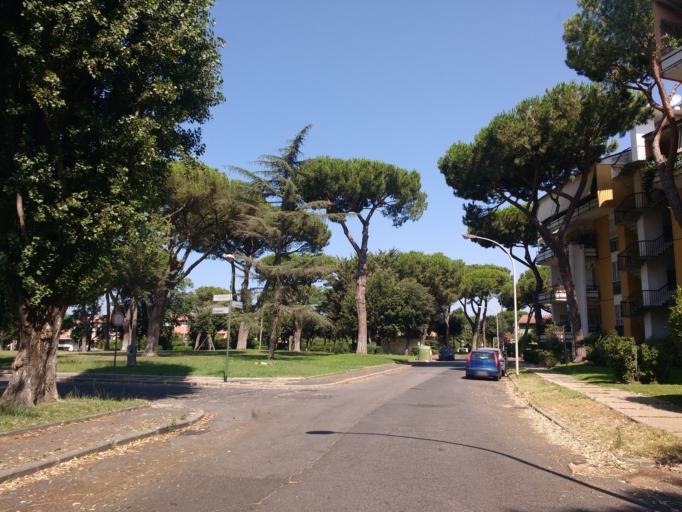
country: IT
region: Latium
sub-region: Citta metropolitana di Roma Capitale
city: Acilia-Castel Fusano-Ostia Antica
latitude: 41.7561
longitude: 12.3554
